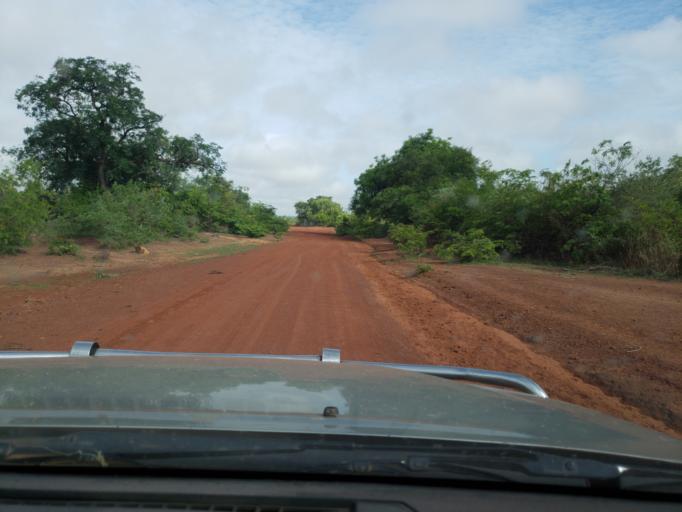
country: ML
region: Sikasso
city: Koutiala
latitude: 12.3927
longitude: -5.9781
